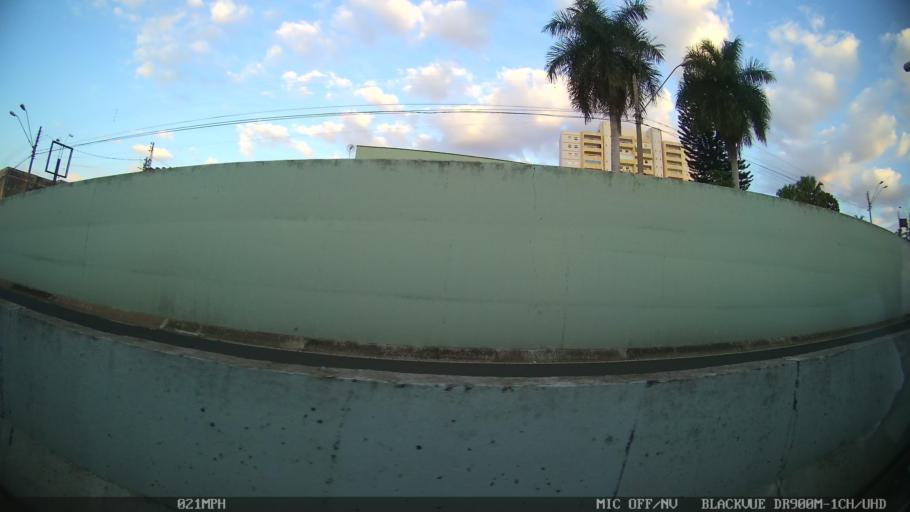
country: BR
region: Sao Paulo
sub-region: Ribeirao Preto
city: Ribeirao Preto
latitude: -21.1732
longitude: -47.7944
